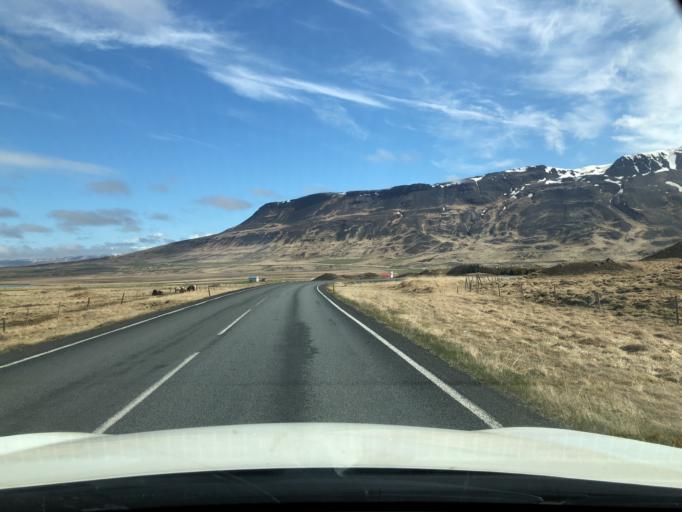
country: IS
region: Northwest
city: Saudarkrokur
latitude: 65.5034
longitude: -20.3898
